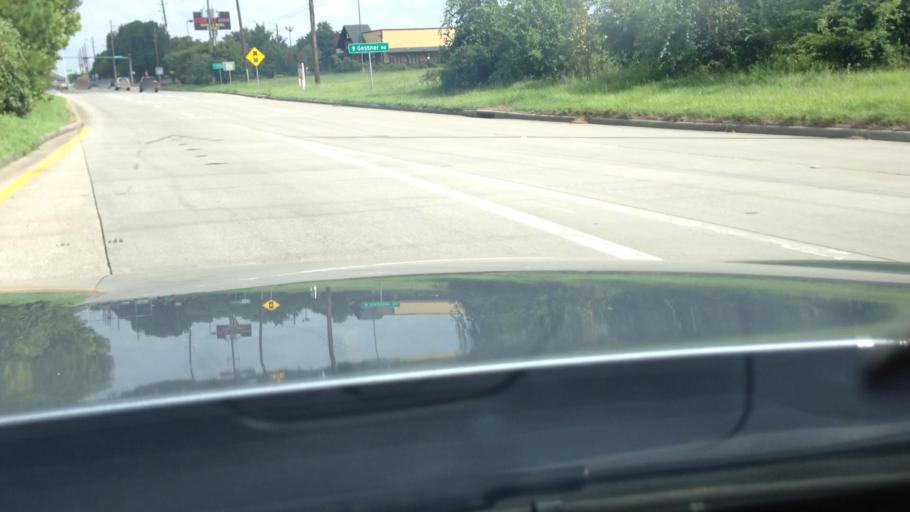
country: US
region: Texas
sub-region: Harris County
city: Hudson
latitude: 29.9523
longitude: -95.5357
